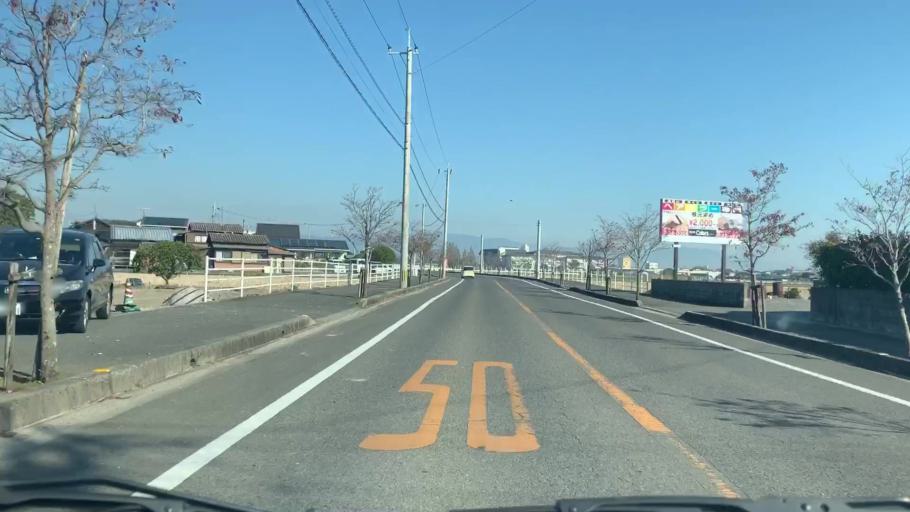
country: JP
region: Saga Prefecture
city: Saga-shi
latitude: 33.2326
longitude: 130.3126
